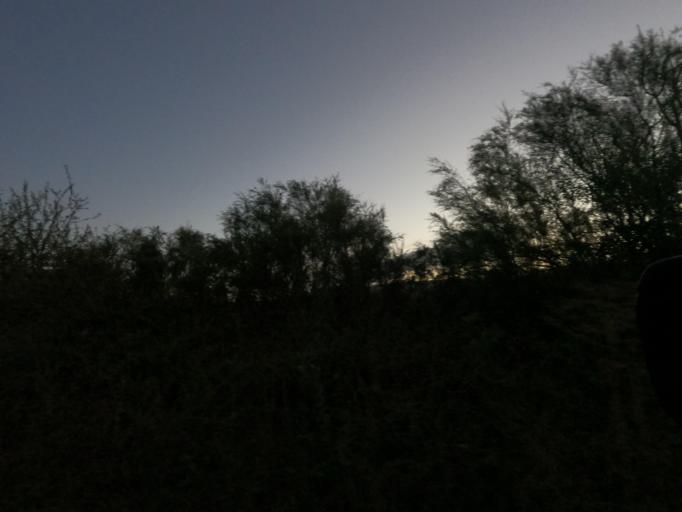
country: CY
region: Pafos
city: Mesogi
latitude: 34.8544
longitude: 32.5420
